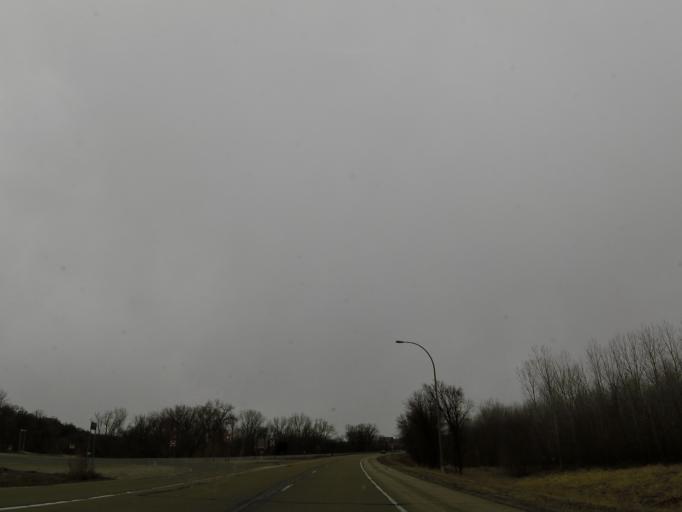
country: US
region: Minnesota
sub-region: Le Sueur County
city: Le Sueur
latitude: 44.4761
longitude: -93.9225
